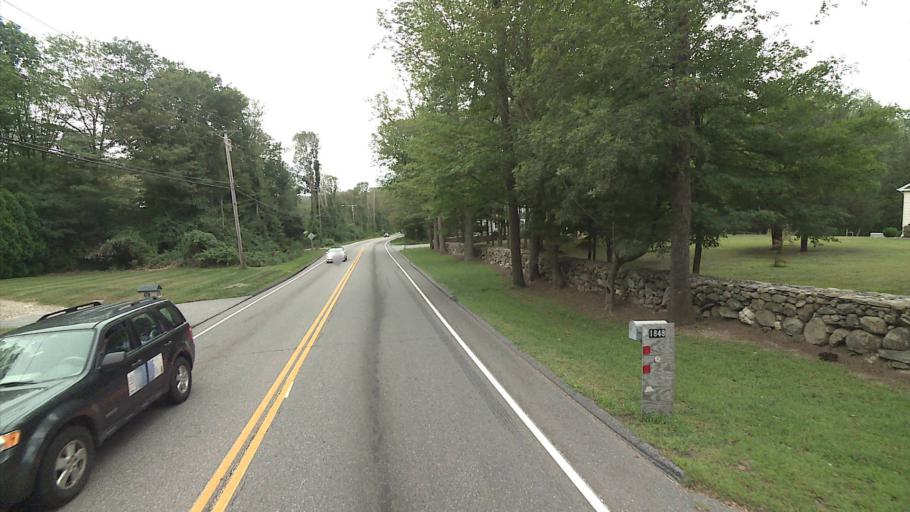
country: US
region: Connecticut
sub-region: New London County
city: Montville Center
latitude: 41.4431
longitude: -72.2297
